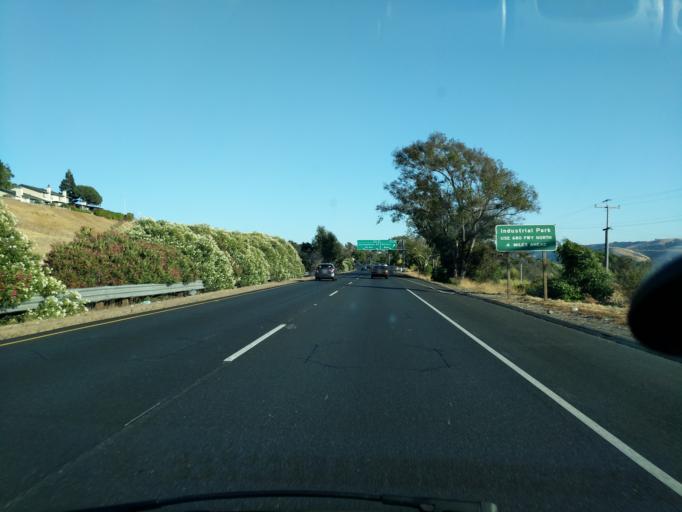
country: US
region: California
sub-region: Contra Costa County
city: Crockett
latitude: 38.0720
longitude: -122.1862
